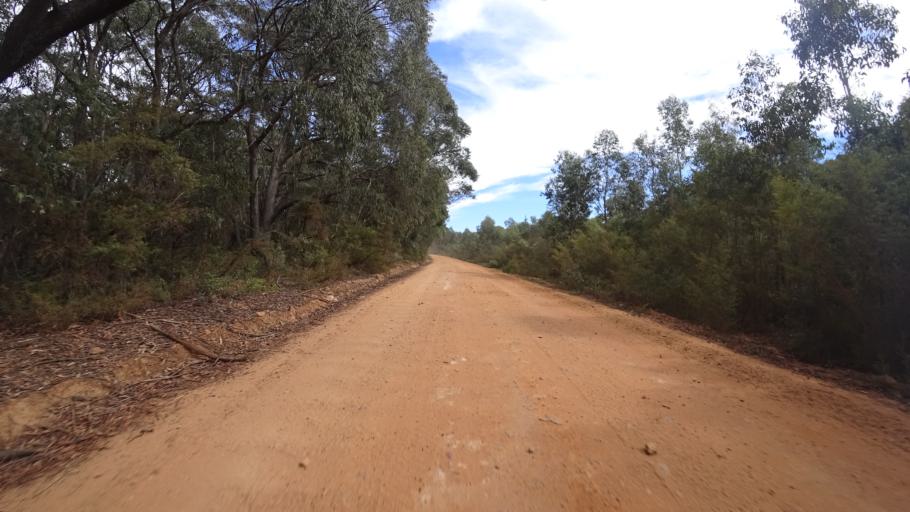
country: AU
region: New South Wales
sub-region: Lithgow
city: Lithgow
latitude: -33.3408
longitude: 150.2520
